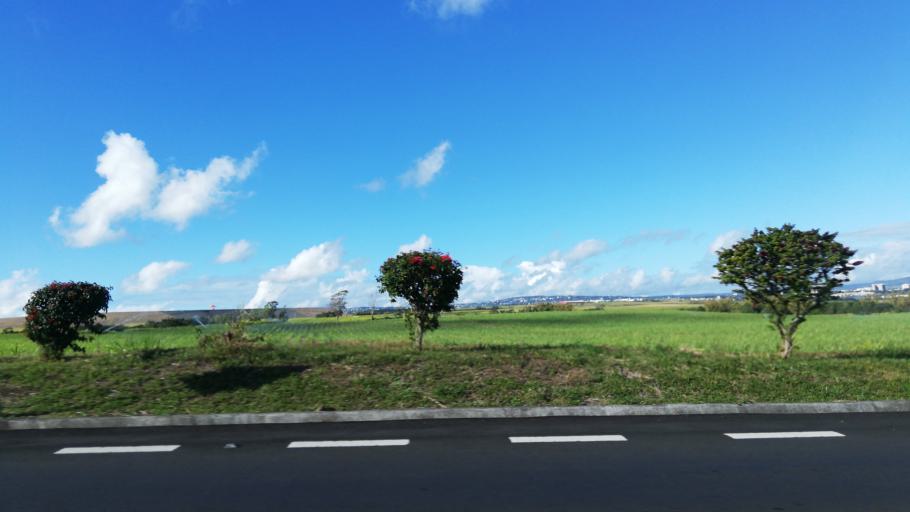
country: MU
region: Moka
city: Saint Pierre
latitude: -20.2338
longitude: 57.5119
